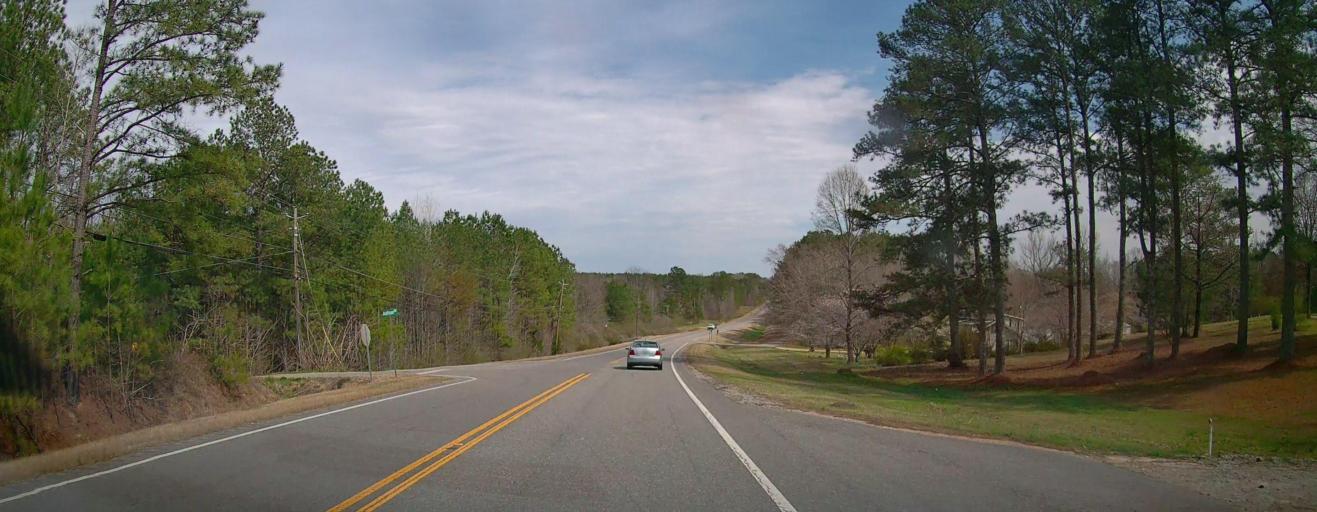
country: US
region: Alabama
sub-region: Walker County
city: Carbon Hill
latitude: 33.9234
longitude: -87.5891
